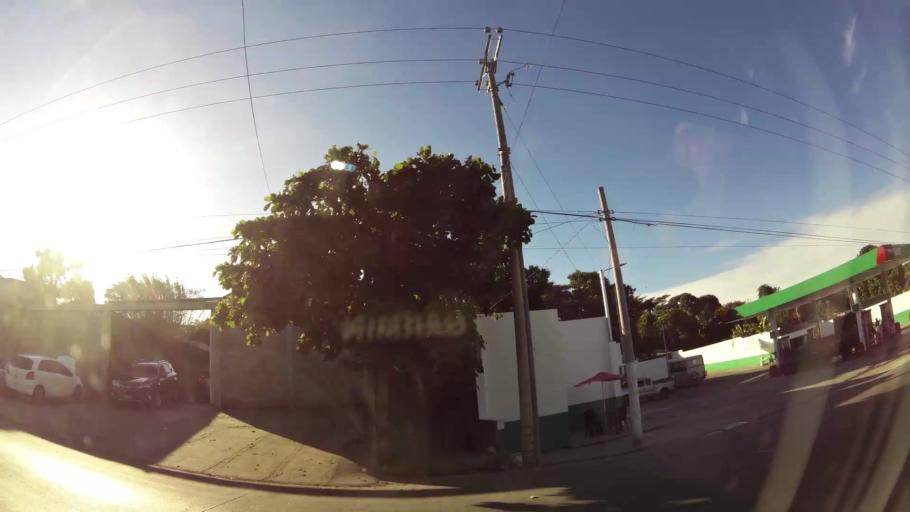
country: SV
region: Santa Ana
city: Metapan
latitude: 14.3204
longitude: -89.4448
